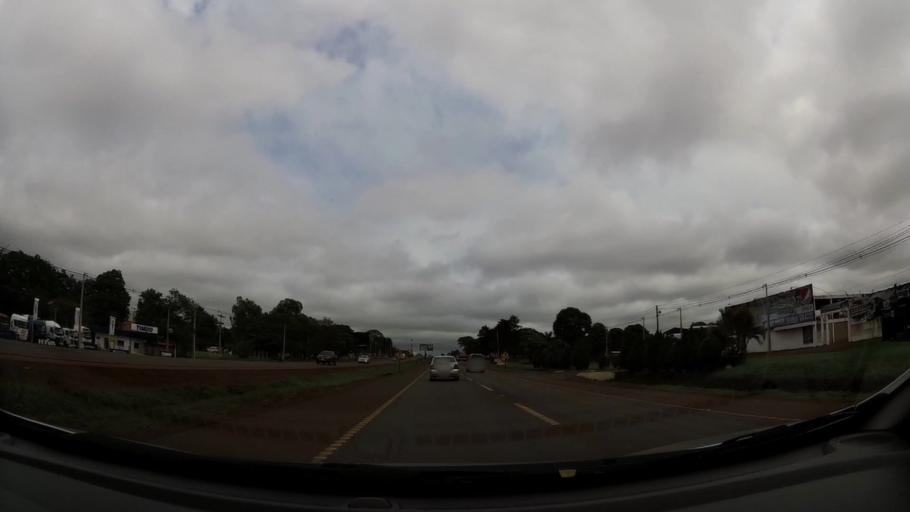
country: PY
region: Alto Parana
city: Ciudad del Este
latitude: -25.4928
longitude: -54.7265
